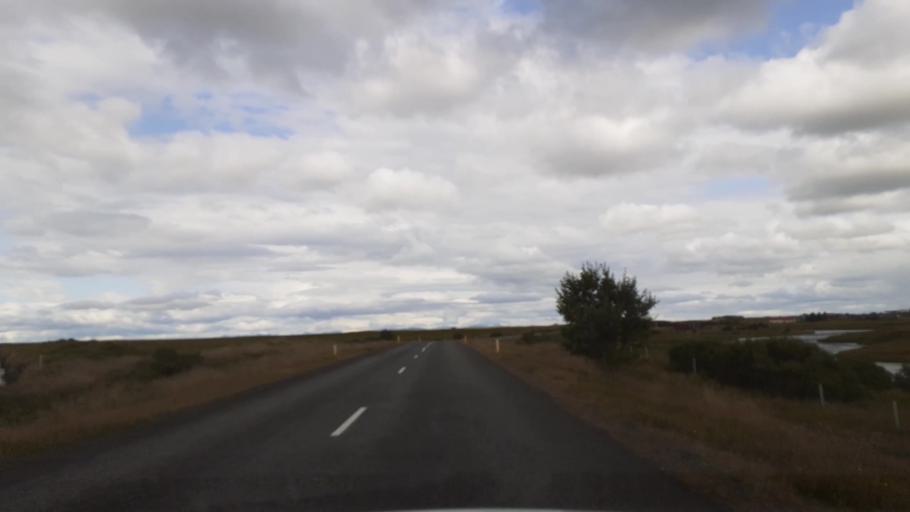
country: IS
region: South
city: Vestmannaeyjar
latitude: 63.8239
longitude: -20.4275
